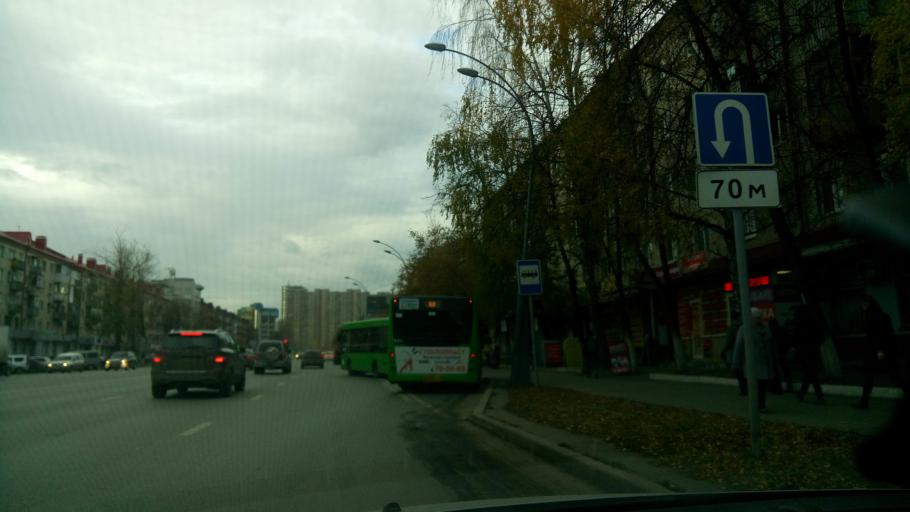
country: RU
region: Tjumen
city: Tyumen
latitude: 57.1409
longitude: 65.5741
